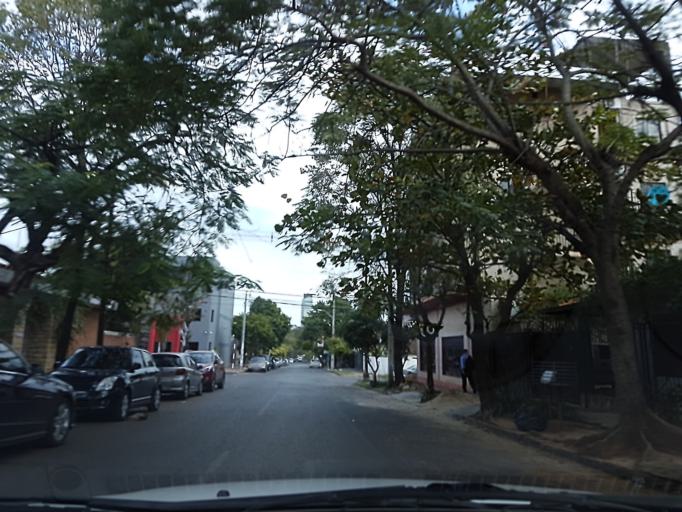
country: PY
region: Asuncion
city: Asuncion
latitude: -25.2911
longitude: -57.5719
